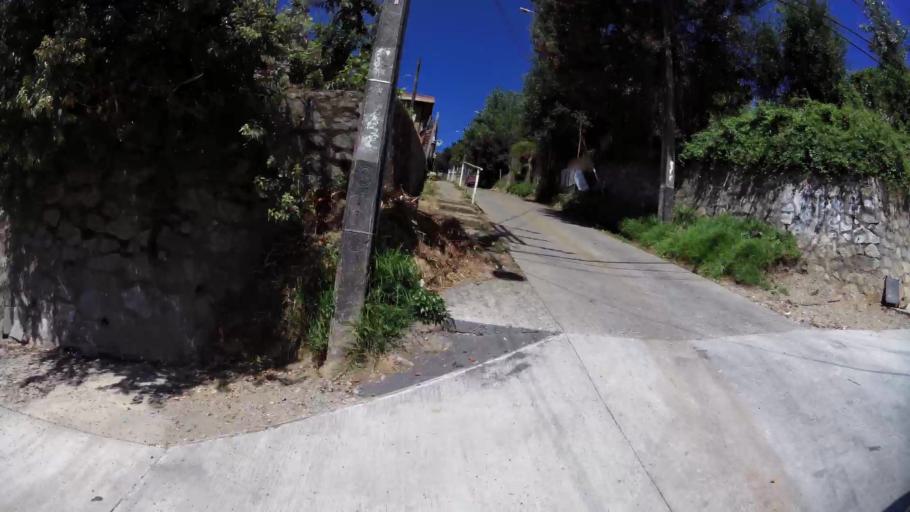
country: CL
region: Biobio
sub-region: Provincia de Concepcion
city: Penco
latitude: -36.7451
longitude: -72.9921
